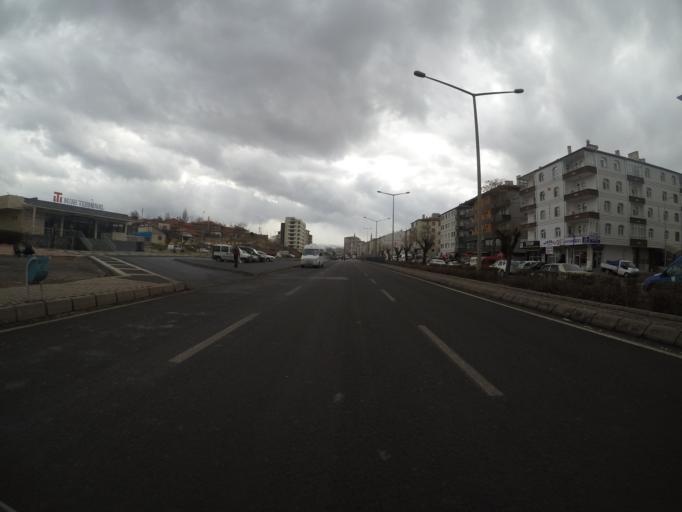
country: TR
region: Kayseri
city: Melikgazi
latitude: 38.7569
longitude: 35.4674
